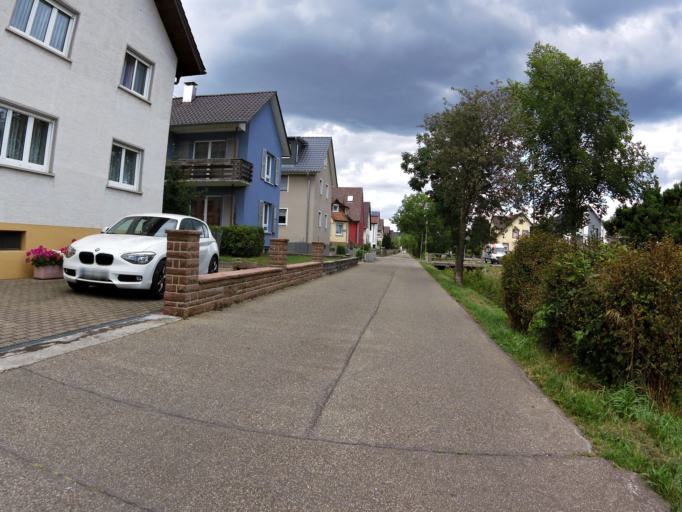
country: DE
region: Baden-Wuerttemberg
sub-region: Freiburg Region
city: Lahr
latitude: 48.3134
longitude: 7.8605
